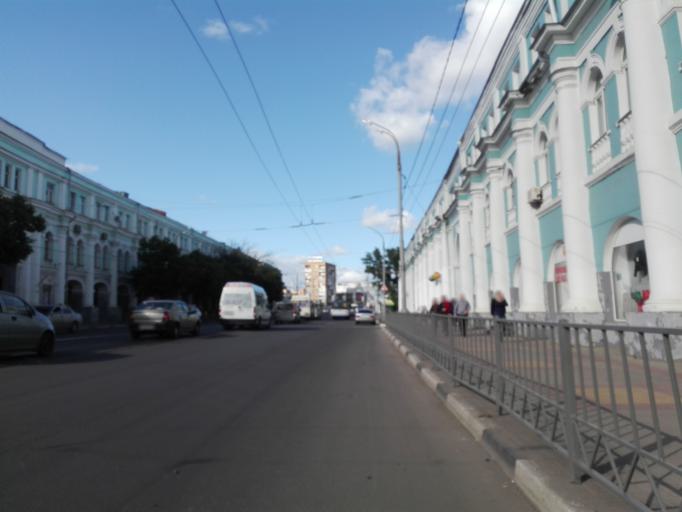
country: RU
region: Orjol
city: Orel
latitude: 52.9641
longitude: 36.0690
